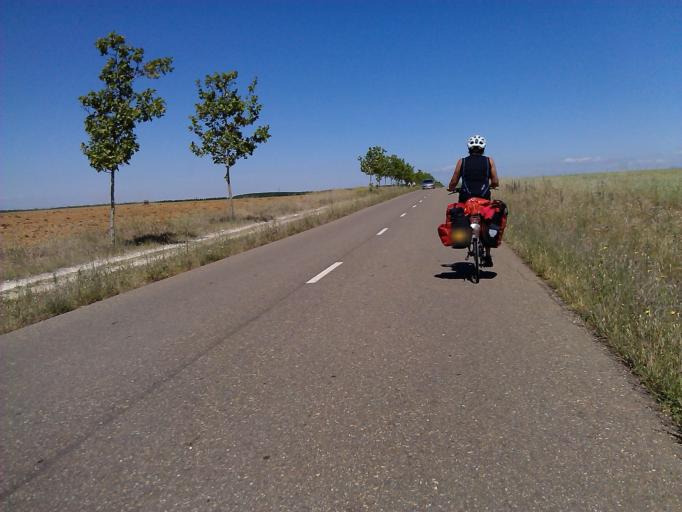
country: ES
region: Castille and Leon
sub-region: Provincia de Leon
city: Villamoratiel de las Matas
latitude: 42.4497
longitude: -5.2719
